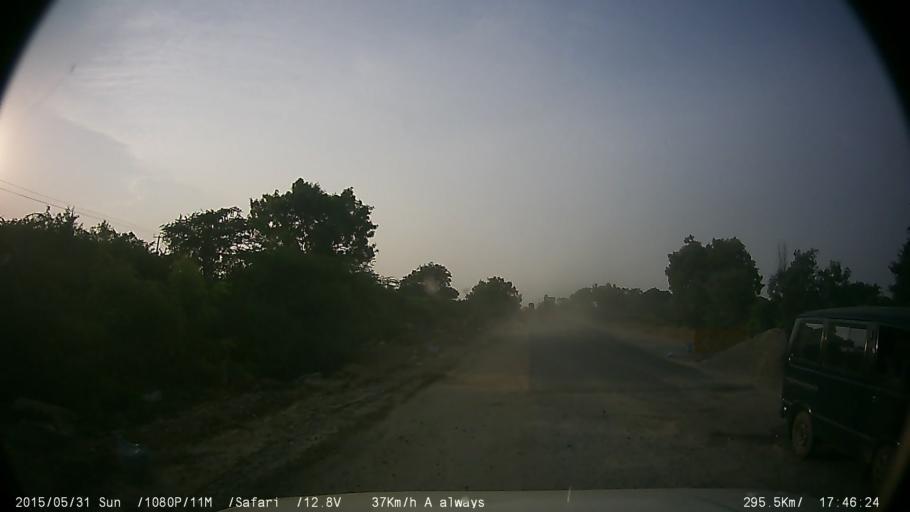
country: IN
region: Karnataka
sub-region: Chamrajnagar
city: Gundlupet
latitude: 11.9570
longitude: 76.6705
